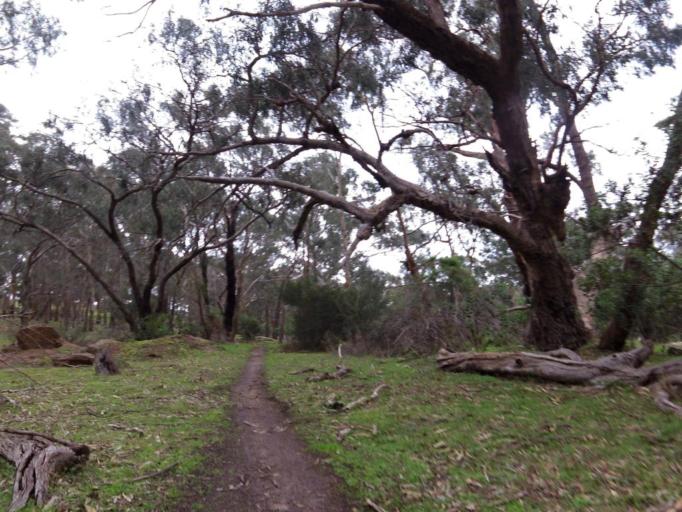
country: AU
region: Victoria
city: Plenty
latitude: -37.6756
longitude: 145.0943
